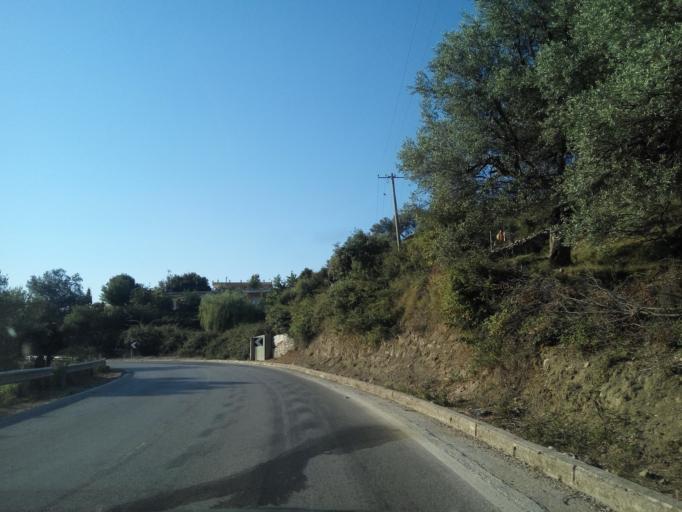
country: AL
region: Vlore
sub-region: Rrethi i Sarandes
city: Lukove
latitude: 39.9572
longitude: 19.9627
